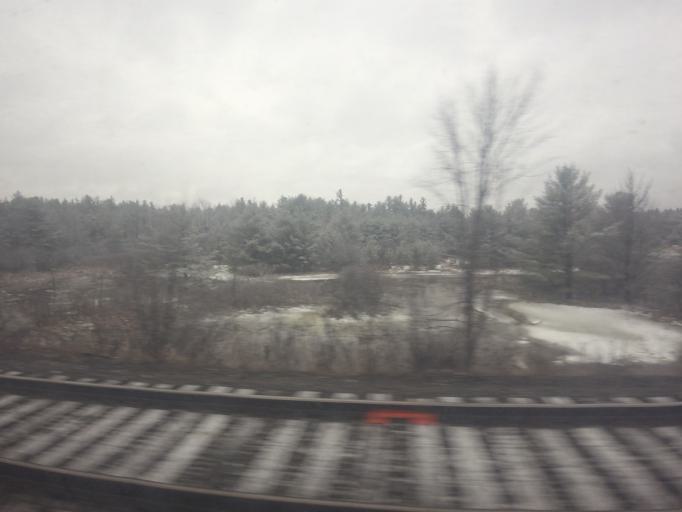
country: US
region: New York
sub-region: Jefferson County
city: Alexandria Bay
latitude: 44.4412
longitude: -75.9544
